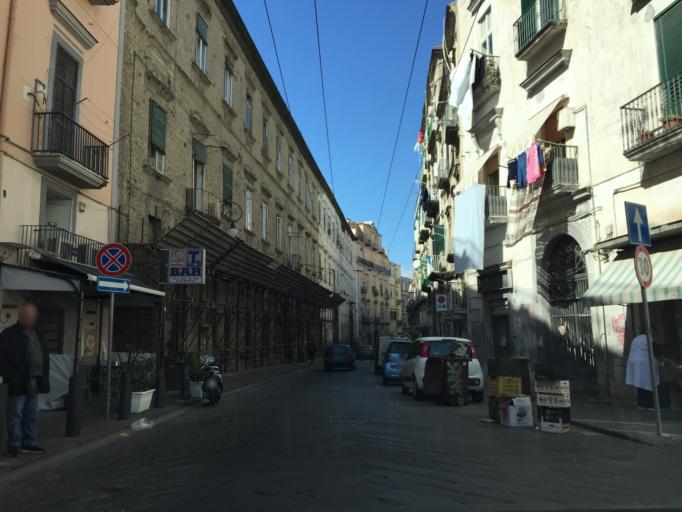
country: IT
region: Campania
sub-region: Provincia di Napoli
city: Portici
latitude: 40.8123
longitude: 14.3411
